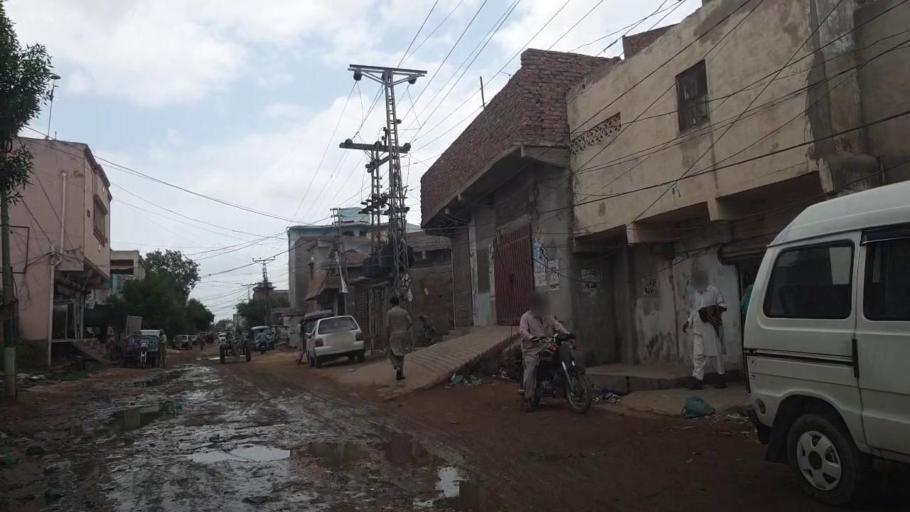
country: PK
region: Sindh
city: Badin
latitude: 24.6564
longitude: 68.8431
